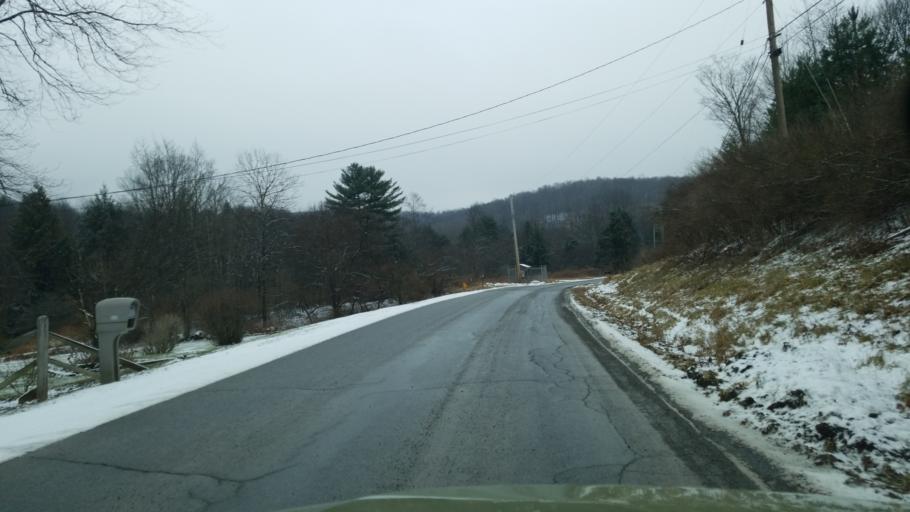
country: US
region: Pennsylvania
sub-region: Jefferson County
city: Sykesville
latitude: 41.0603
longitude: -78.8197
